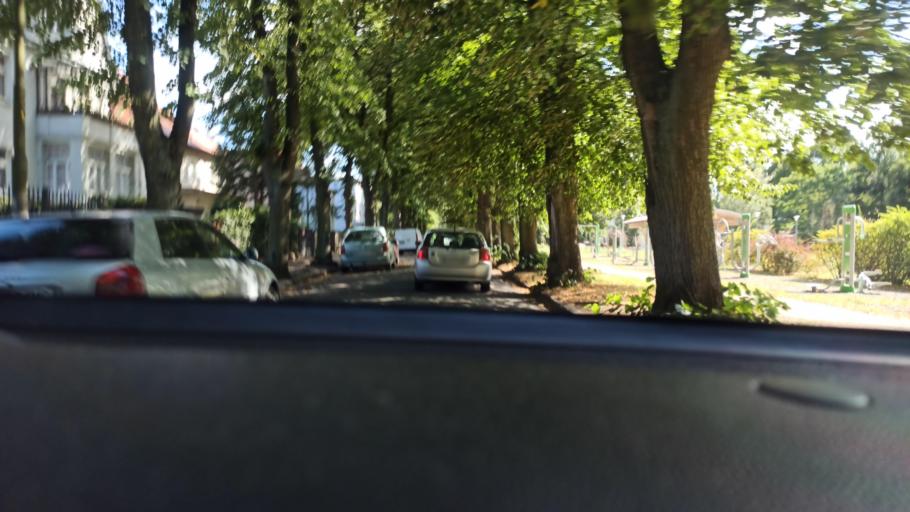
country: PL
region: West Pomeranian Voivodeship
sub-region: Szczecin
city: Szczecin
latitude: 53.4407
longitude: 14.5058
